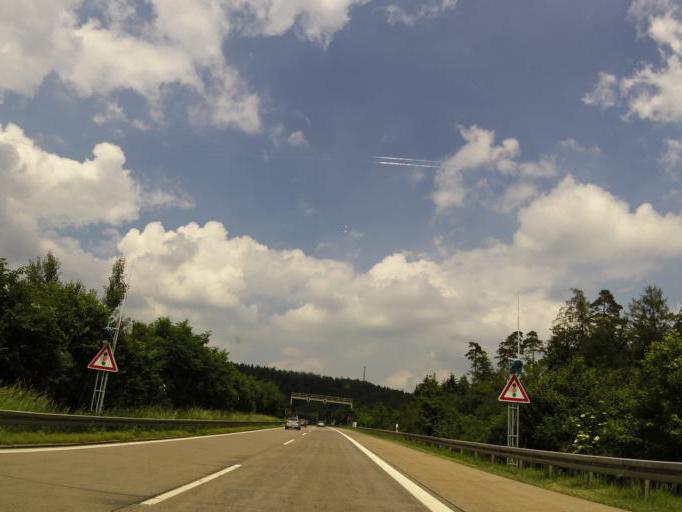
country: DE
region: Baden-Wuerttemberg
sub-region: Regierungsbezirk Stuttgart
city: Ellenberg
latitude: 49.0150
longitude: 10.1969
